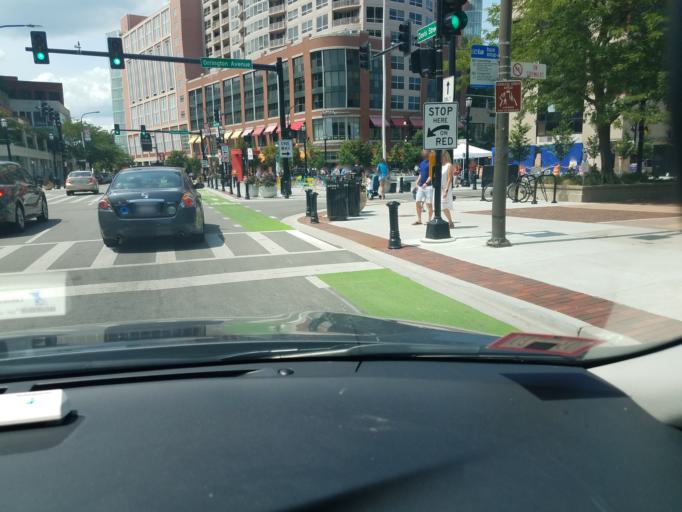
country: US
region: Illinois
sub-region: Cook County
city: Evanston
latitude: 42.0466
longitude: -87.6812
